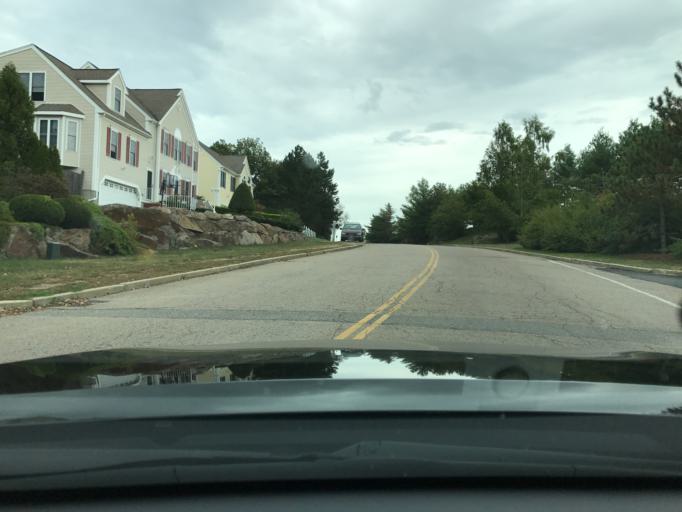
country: US
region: Massachusetts
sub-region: Norfolk County
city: Braintree
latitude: 42.2381
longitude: -70.9884
